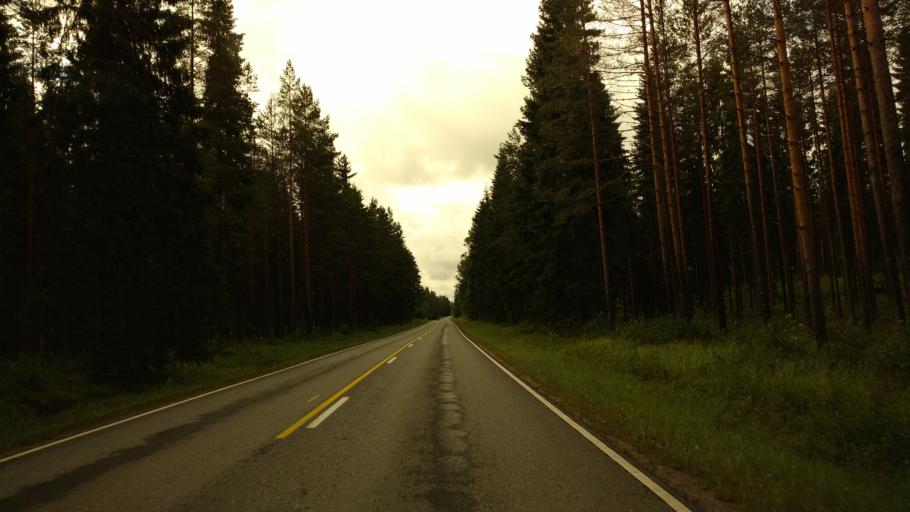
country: FI
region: Varsinais-Suomi
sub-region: Loimaa
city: Koski Tl
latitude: 60.6120
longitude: 23.1194
